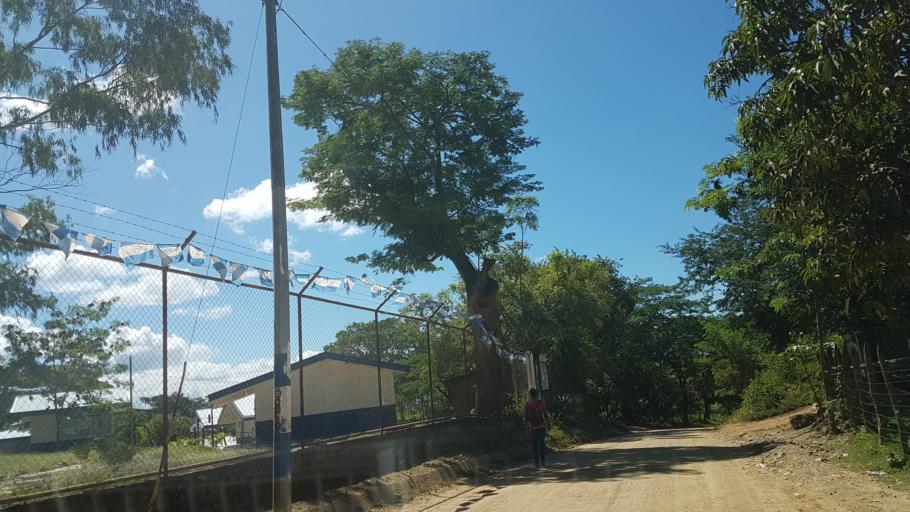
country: HN
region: El Paraiso
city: Santa Cruz
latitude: 13.7357
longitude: -86.6730
